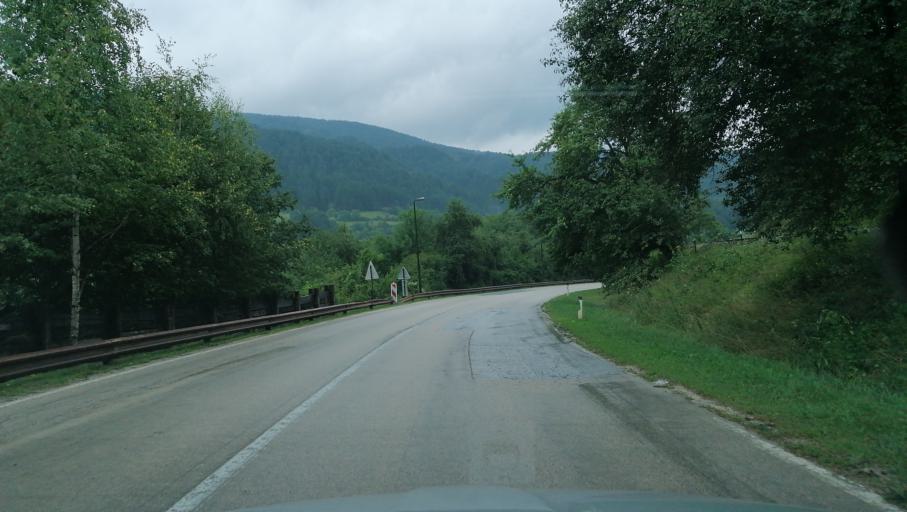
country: RS
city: Durici
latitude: 43.7953
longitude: 19.5121
